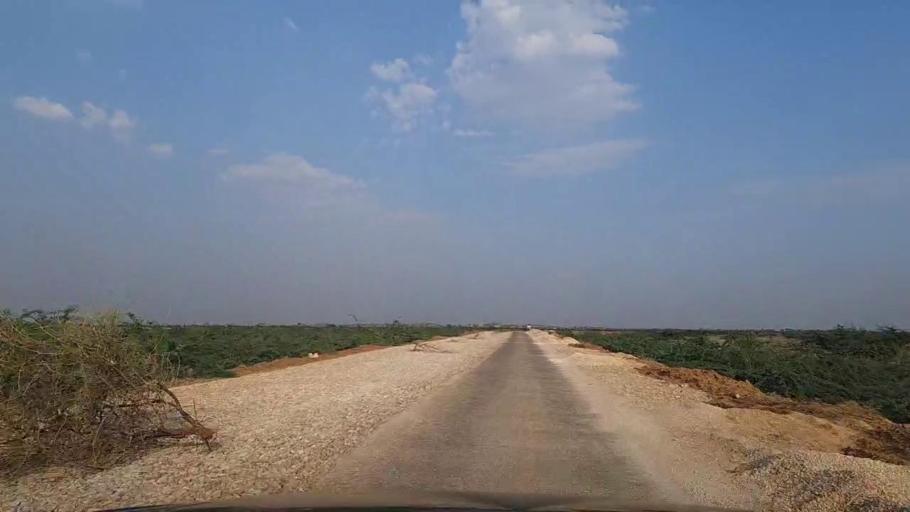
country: PK
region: Sindh
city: Gharo
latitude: 24.8462
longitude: 67.7470
